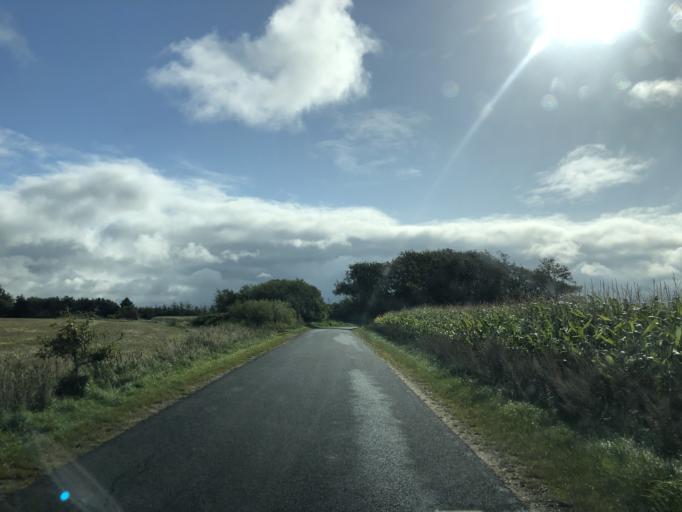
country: DK
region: Central Jutland
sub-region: Holstebro Kommune
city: Ulfborg
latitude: 56.3010
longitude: 8.4589
